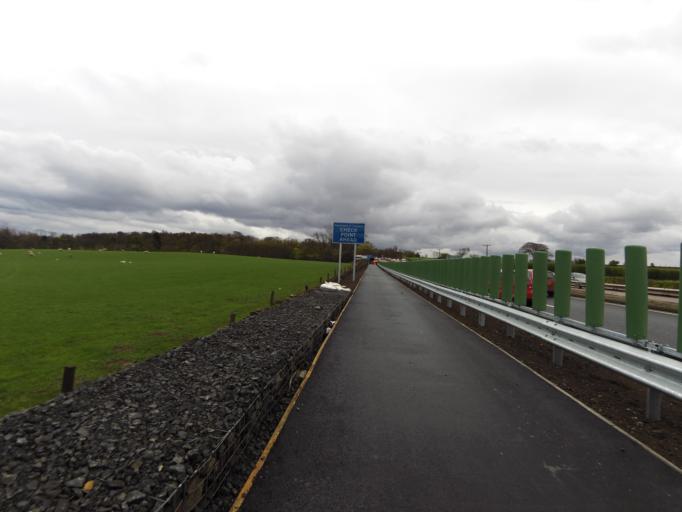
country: GB
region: Scotland
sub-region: Edinburgh
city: Queensferry
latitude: 55.9770
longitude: -3.3407
